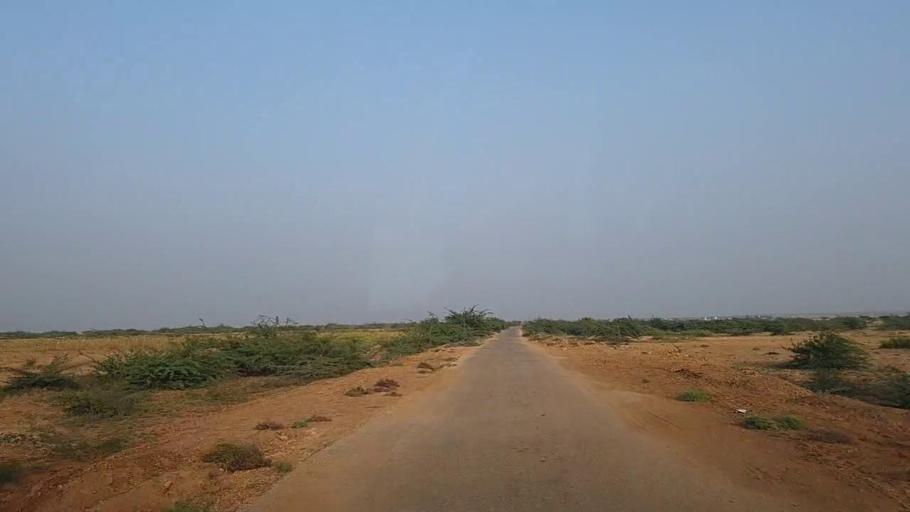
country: PK
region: Sindh
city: Thatta
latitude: 24.6906
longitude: 67.8305
